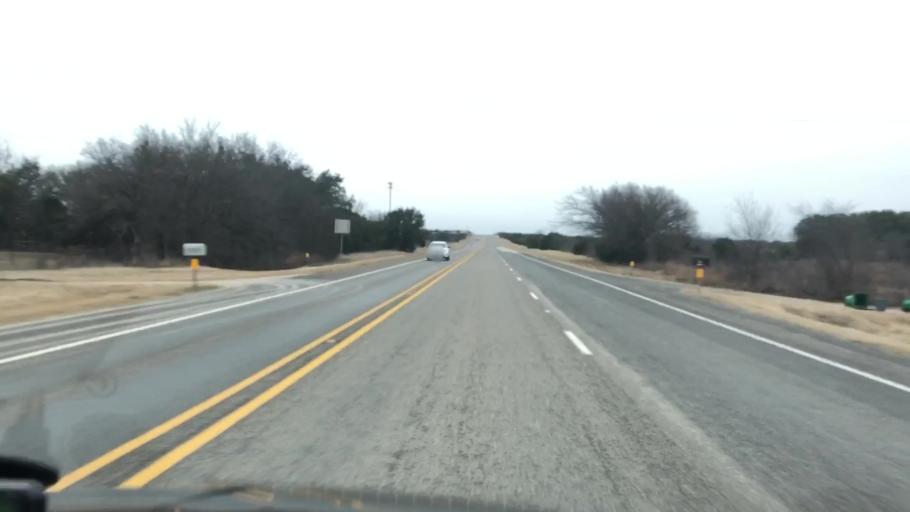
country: US
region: Texas
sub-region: Lampasas County
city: Lampasas
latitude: 31.1739
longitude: -98.1741
